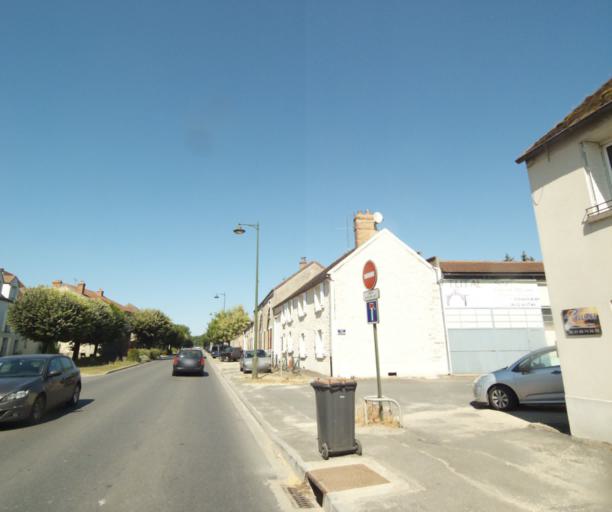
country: FR
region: Ile-de-France
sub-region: Departement de Seine-et-Marne
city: La Chapelle-la-Reine
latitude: 48.3184
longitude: 2.5727
